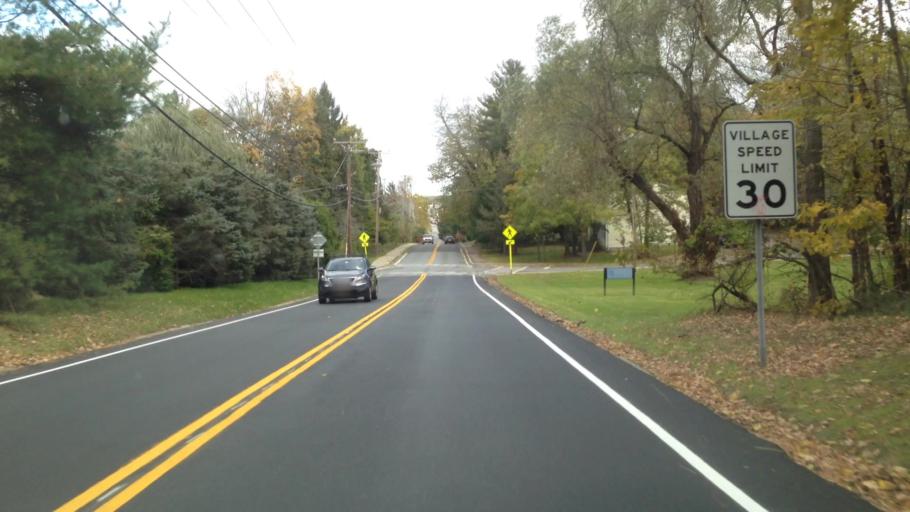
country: US
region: New York
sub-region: Ulster County
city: New Paltz
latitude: 41.7420
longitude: -74.0894
